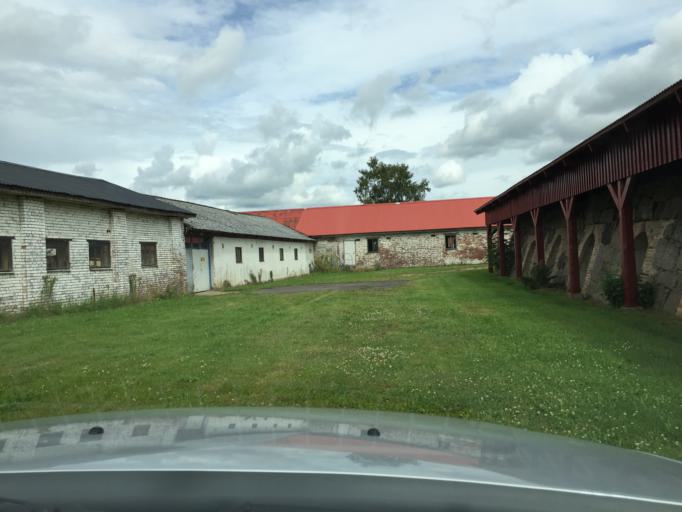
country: SE
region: Skane
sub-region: Hassleholms Kommun
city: Sosdala
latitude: 56.0090
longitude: 13.6399
